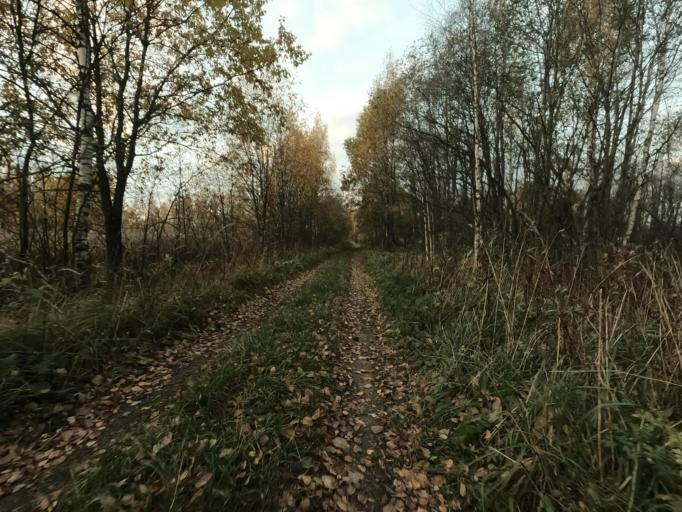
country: RU
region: Leningrad
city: Mga
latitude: 59.8224
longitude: 31.1779
